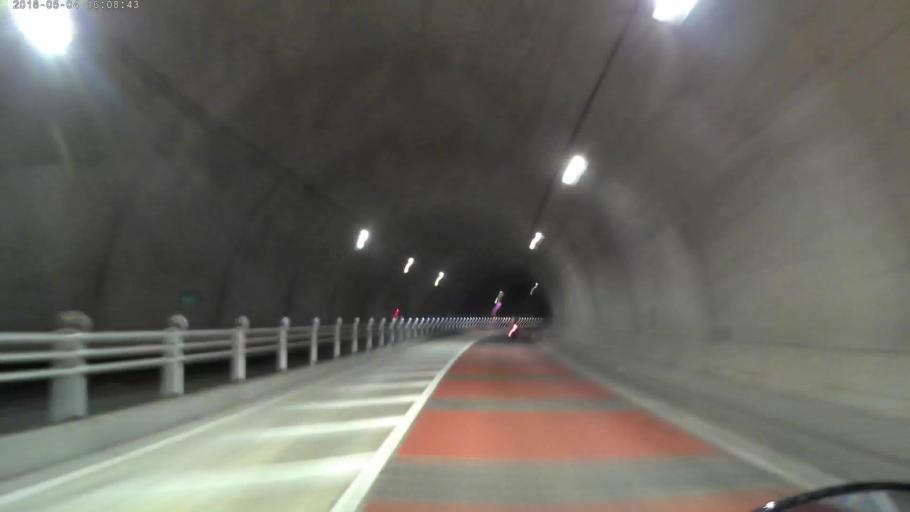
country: JP
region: Kanagawa
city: Yokohama
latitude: 35.4939
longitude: 139.6596
